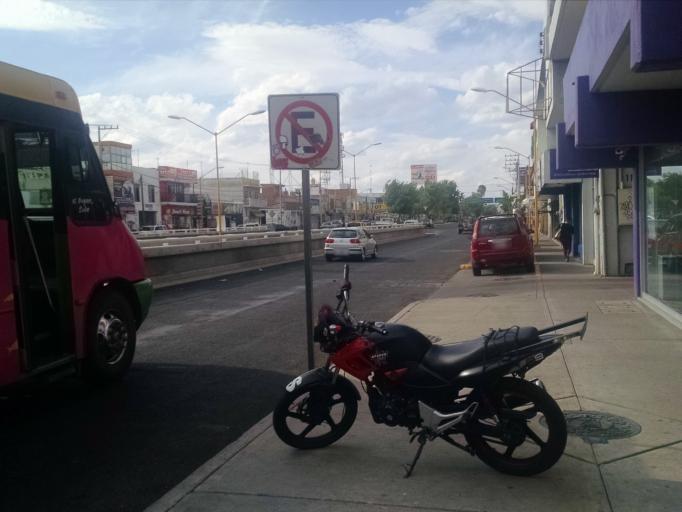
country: MX
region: Aguascalientes
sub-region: Aguascalientes
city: Aguascalientes
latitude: 21.8755
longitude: -102.3120
